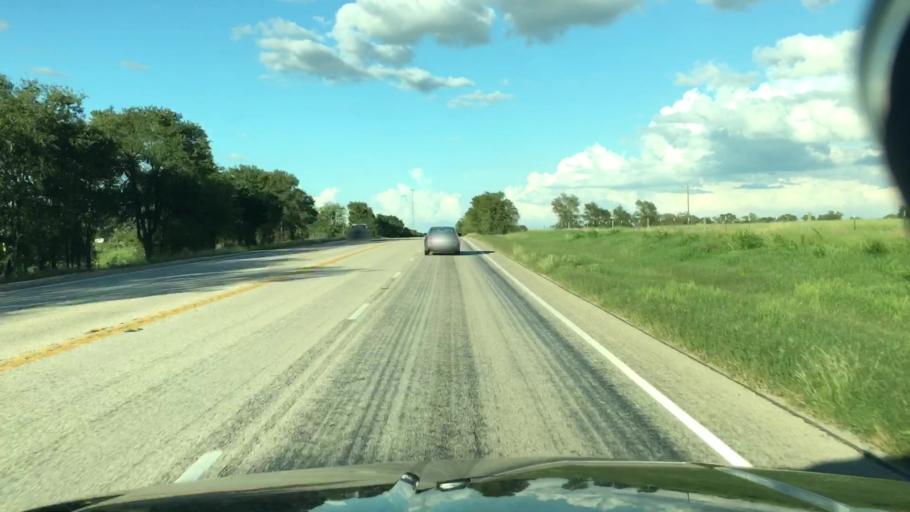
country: US
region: Texas
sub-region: Lee County
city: Lexington
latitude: 30.3257
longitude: -96.9211
